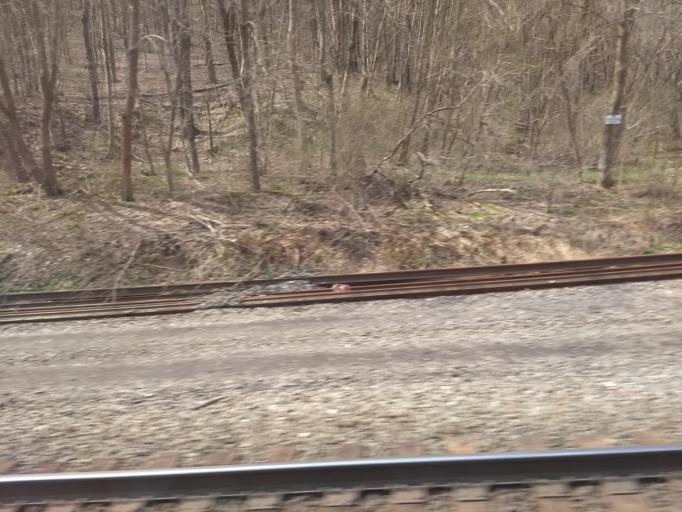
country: US
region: Pennsylvania
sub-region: Blair County
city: Tyrone
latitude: 40.6652
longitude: -78.2293
